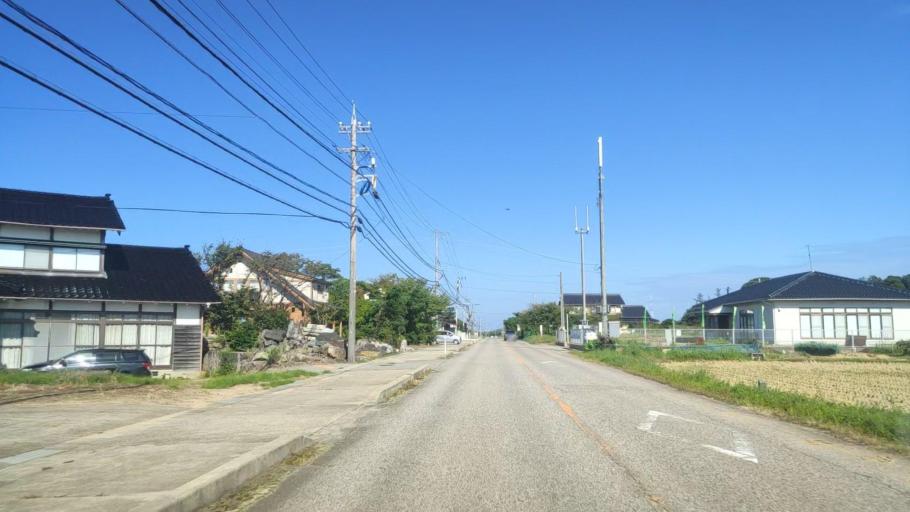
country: JP
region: Ishikawa
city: Hakui
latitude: 37.0363
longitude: 136.7452
